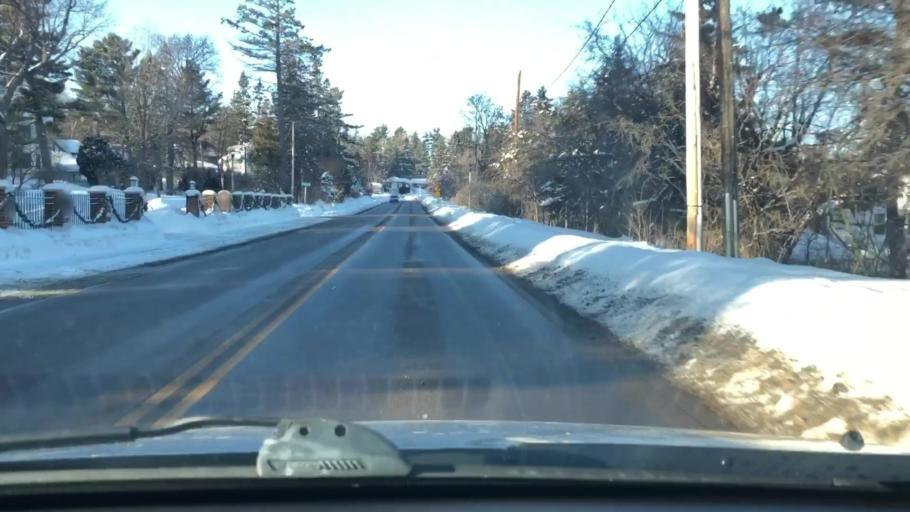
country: US
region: Minnesota
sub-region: Saint Louis County
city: Duluth
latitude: 46.8171
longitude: -92.0693
